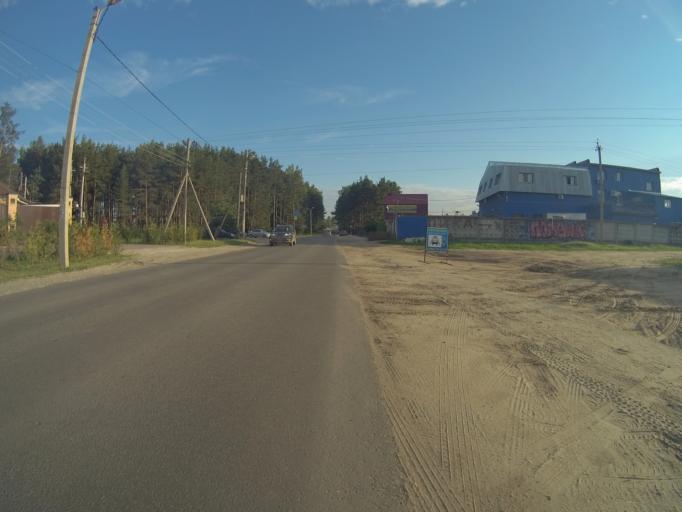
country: RU
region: Vladimir
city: Kommunar
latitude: 56.1151
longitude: 40.4504
